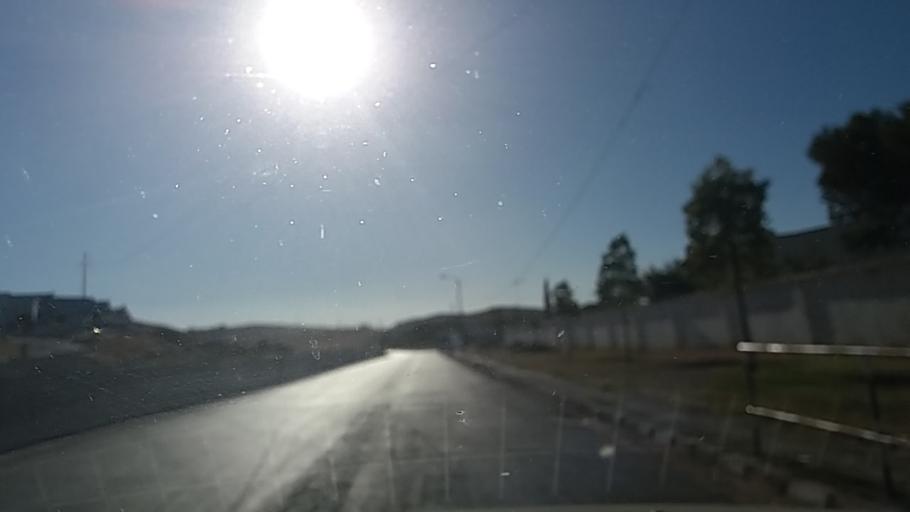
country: MA
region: Tanger-Tetouan
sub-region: Tanger-Assilah
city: Tangier
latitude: 35.7342
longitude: -5.7679
